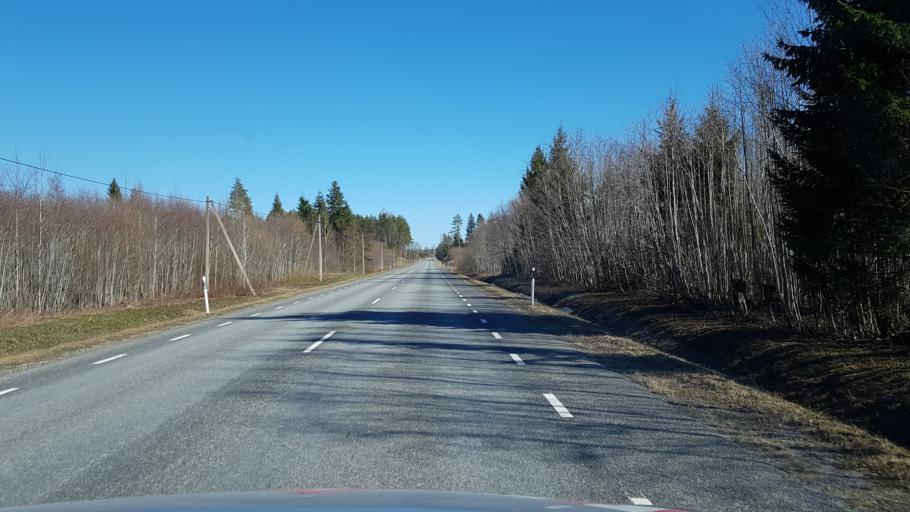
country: EE
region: Ida-Virumaa
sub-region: Aseri vald
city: Aseri
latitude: 59.3523
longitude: 26.7439
